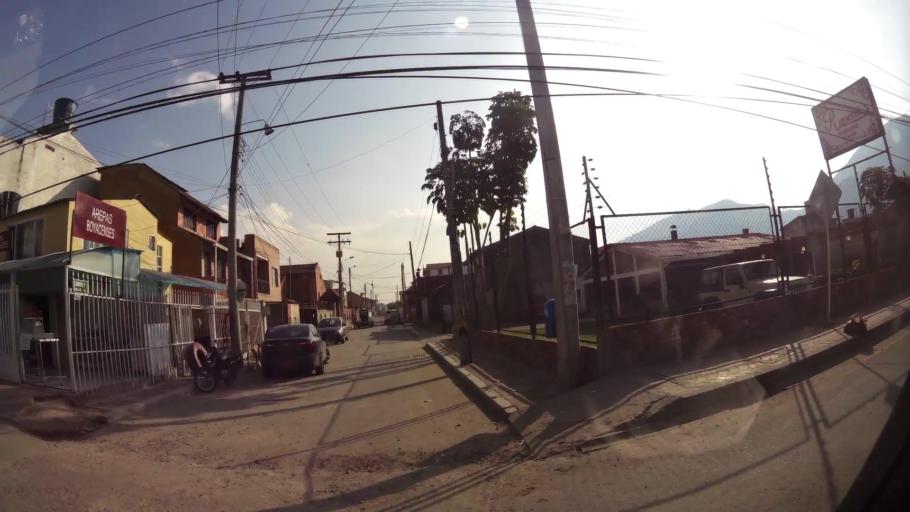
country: CO
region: Cundinamarca
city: Cota
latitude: 4.8077
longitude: -74.1011
